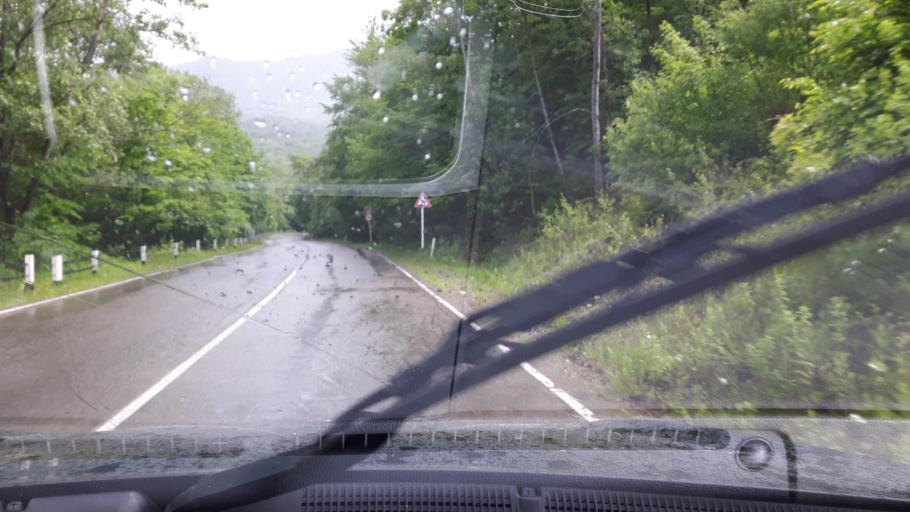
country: GE
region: Kakheti
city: Sagarejo
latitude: 41.8661
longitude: 45.3496
